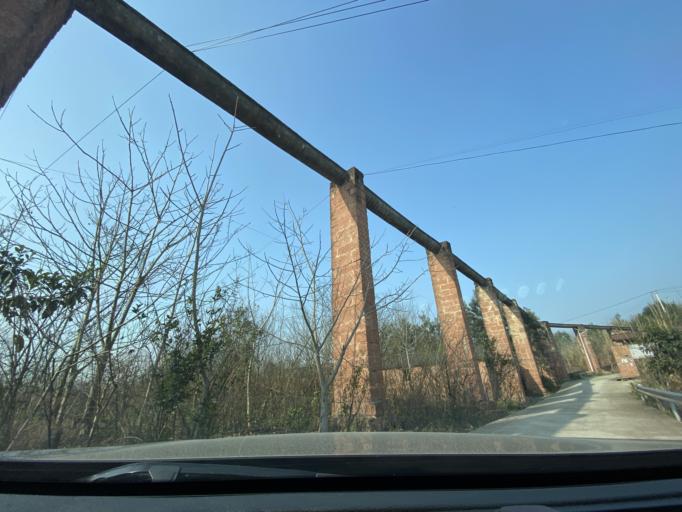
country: CN
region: Sichuan
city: Wenlin
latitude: 30.2520
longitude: 104.2531
